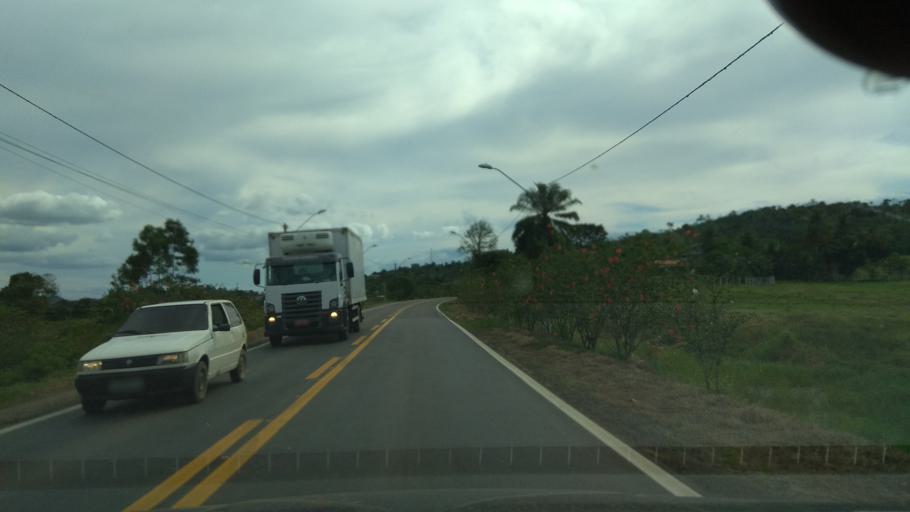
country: BR
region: Bahia
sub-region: Ubata
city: Ubata
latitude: -14.2094
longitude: -39.5871
